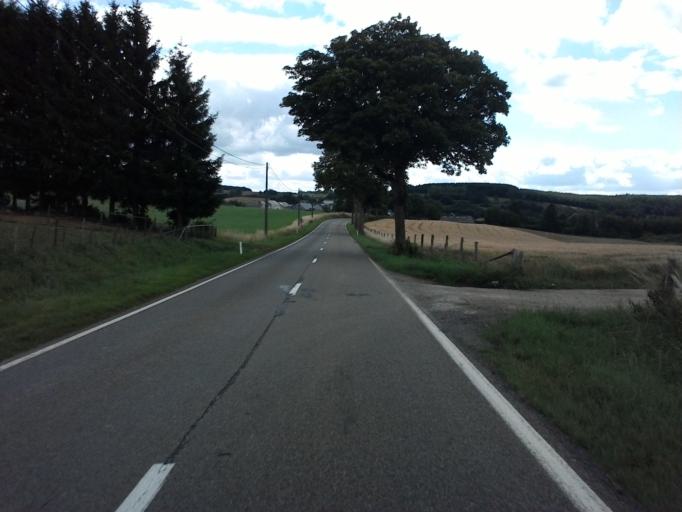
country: BE
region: Wallonia
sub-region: Province du Luxembourg
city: Leglise
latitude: 49.8049
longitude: 5.5280
